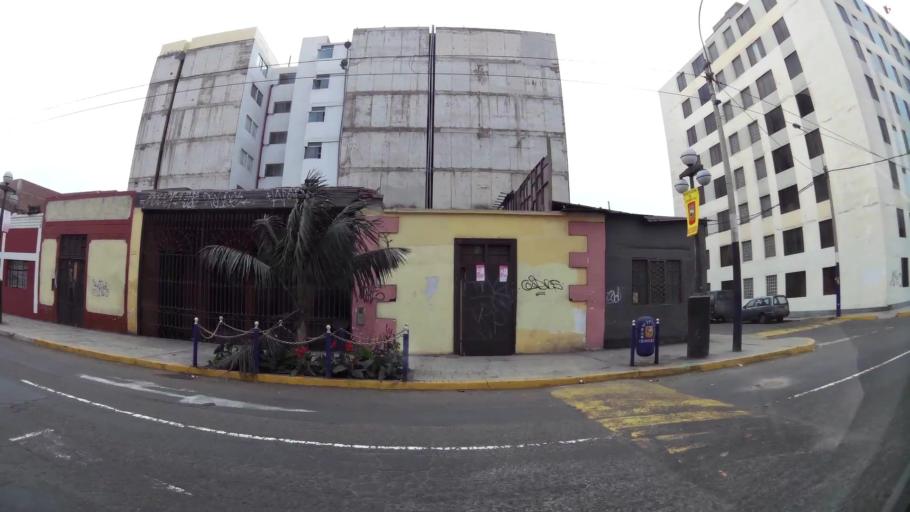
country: PE
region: Lima
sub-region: Lima
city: Surco
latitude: -12.1659
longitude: -77.0232
